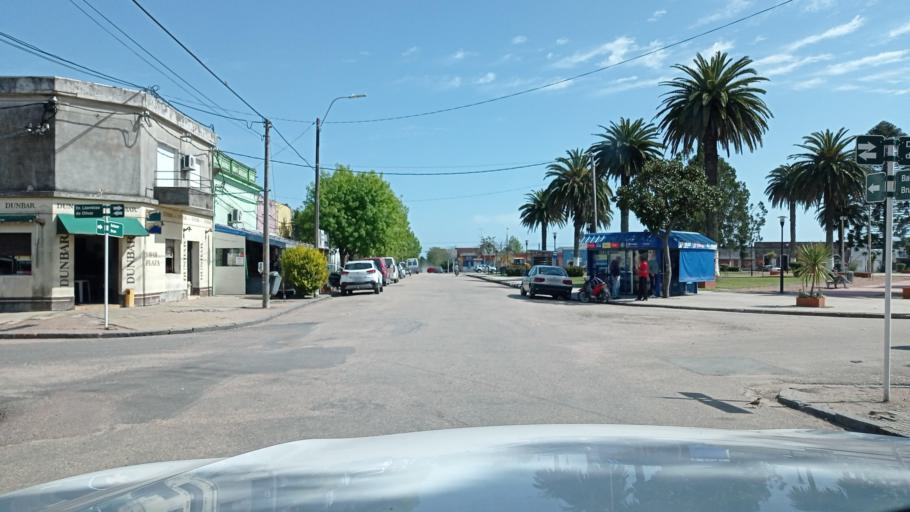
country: UY
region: Canelones
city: Santa Rosa
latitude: -34.4992
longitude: -56.0410
